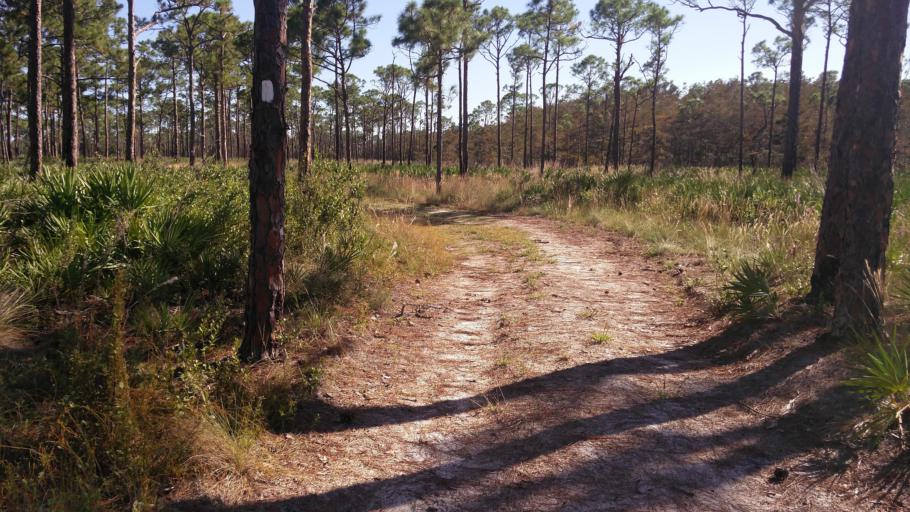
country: US
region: Florida
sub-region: Palm Beach County
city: Tequesta
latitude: 27.0081
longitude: -80.1238
